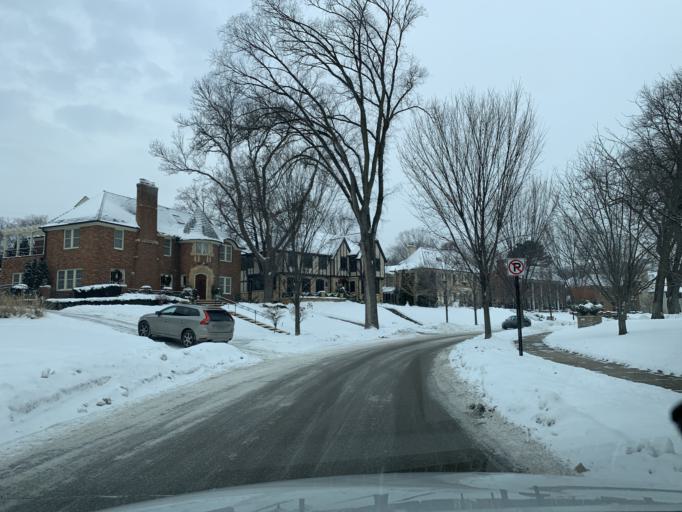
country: US
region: Minnesota
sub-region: Hennepin County
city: Edina
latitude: 44.9140
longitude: -93.3414
